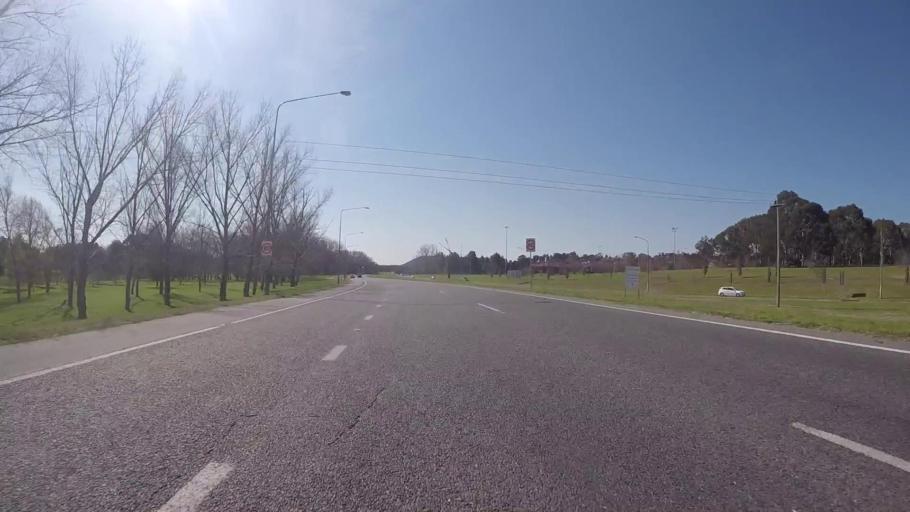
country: AU
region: Australian Capital Territory
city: Forrest
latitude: -35.3343
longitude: 149.0860
